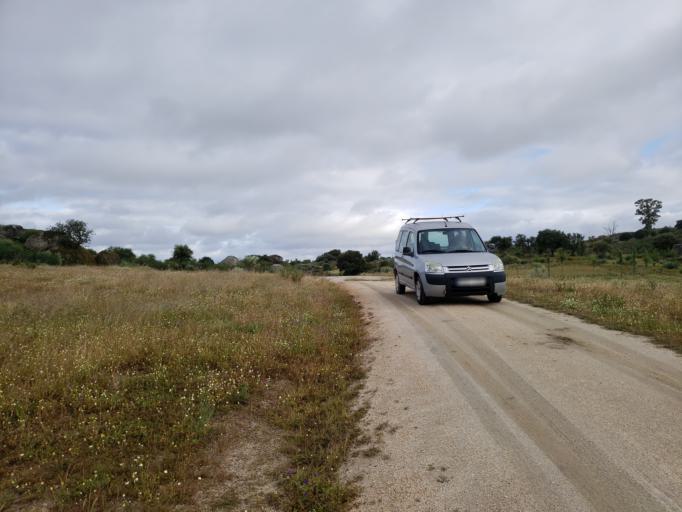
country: ES
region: Extremadura
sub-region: Provincia de Caceres
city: Malpartida de Caceres
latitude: 39.4246
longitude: -6.4871
